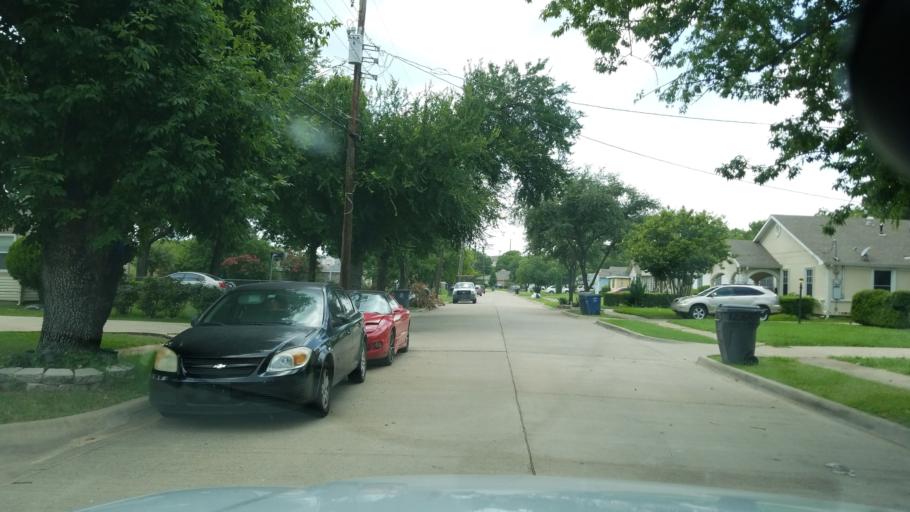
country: US
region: Texas
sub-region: Dallas County
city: Dallas
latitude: 32.8143
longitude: -96.8619
